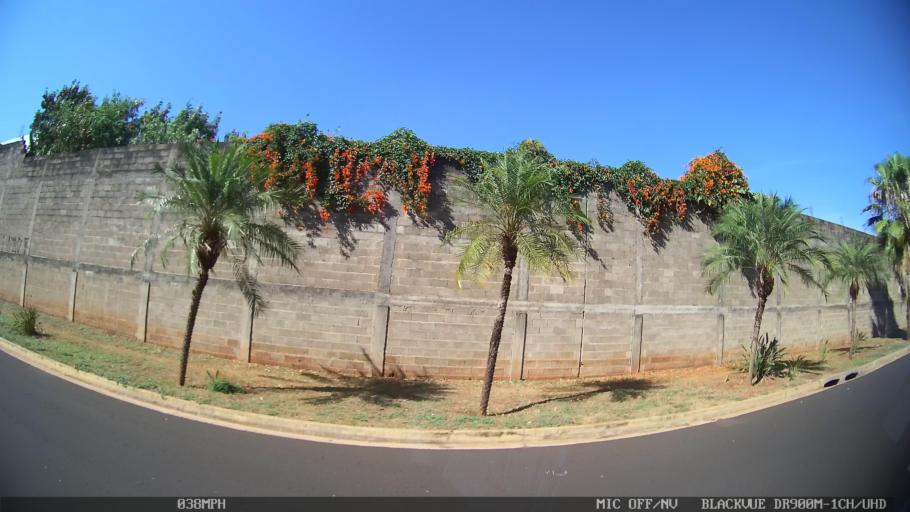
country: BR
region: Sao Paulo
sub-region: Ribeirao Preto
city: Ribeirao Preto
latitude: -21.2211
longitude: -47.7623
